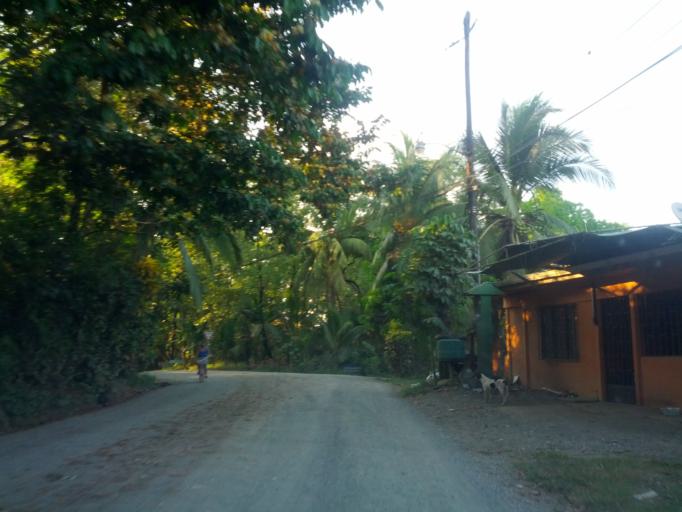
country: CR
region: Puntarenas
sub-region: Canton de Golfito
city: Golfito
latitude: 8.5358
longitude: -83.3029
